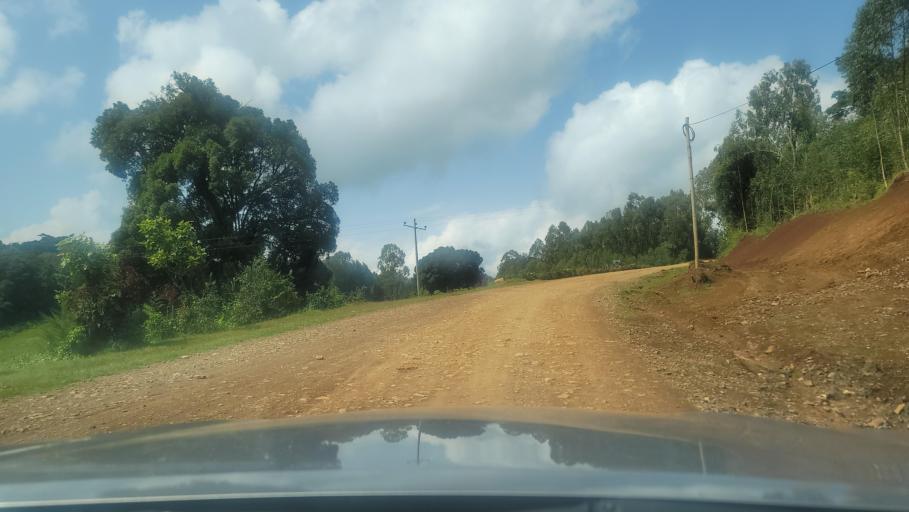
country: ET
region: Oromiya
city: Agaro
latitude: 7.7957
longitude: 36.4548
